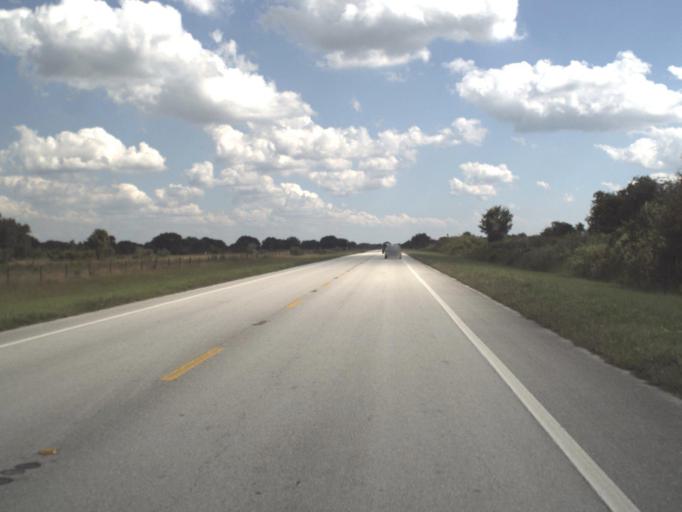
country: US
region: Florida
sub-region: Highlands County
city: Lake Placid
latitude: 27.4198
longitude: -81.2038
